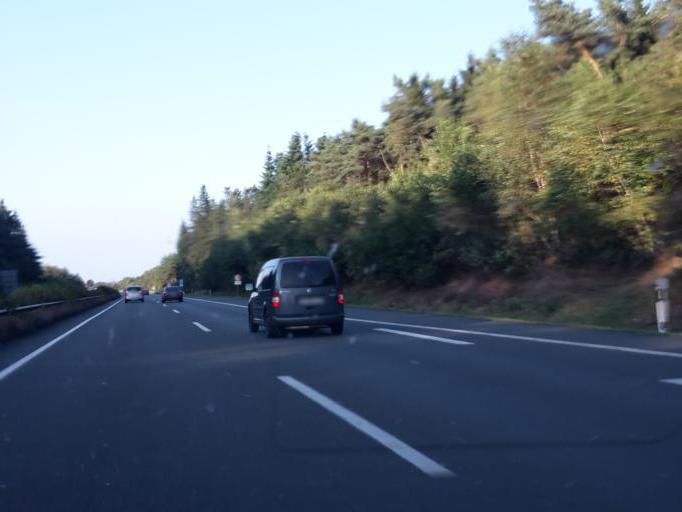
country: DE
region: Lower Saxony
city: Holdorf
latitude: 52.5445
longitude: 8.1141
